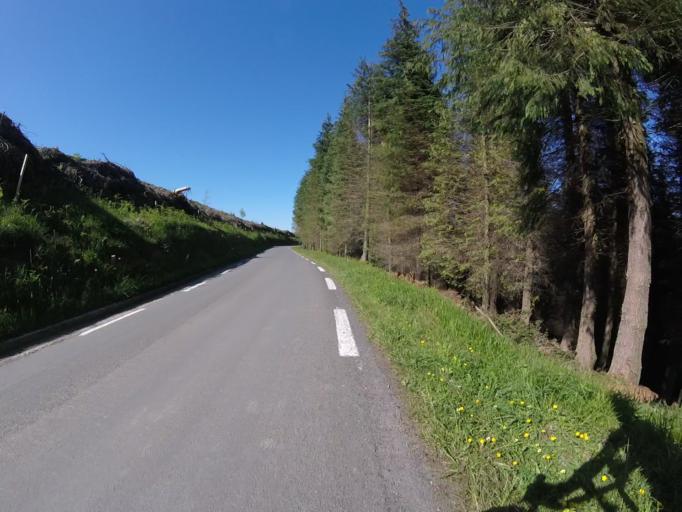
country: ES
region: Basque Country
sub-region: Provincia de Guipuzcoa
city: Errezil
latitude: 43.2013
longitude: -2.1992
